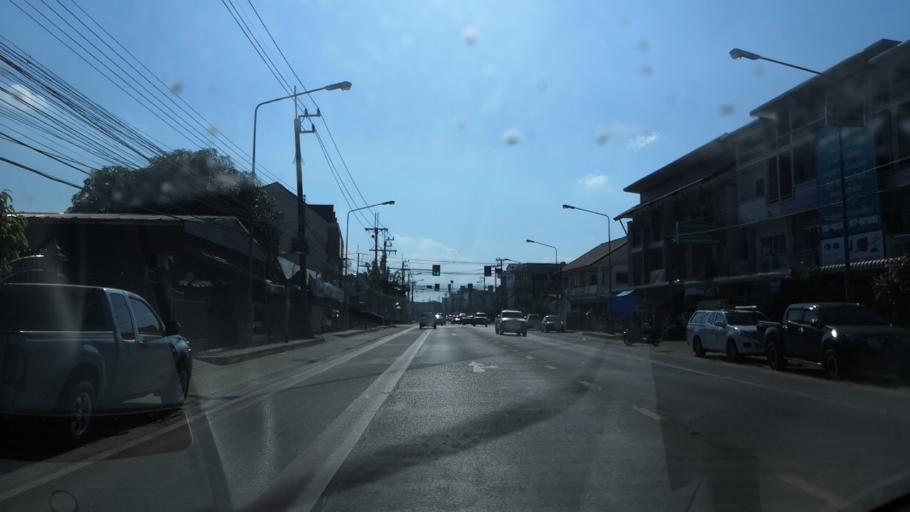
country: TH
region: Chiang Rai
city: Chiang Rai
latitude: 19.9269
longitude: 99.8373
